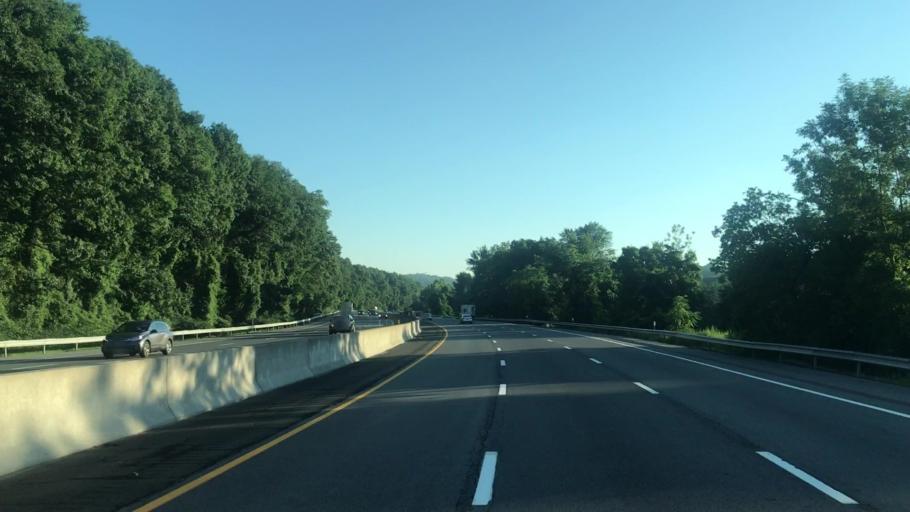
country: US
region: New York
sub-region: Westchester County
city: Ardsley
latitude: 41.0150
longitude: -73.8471
